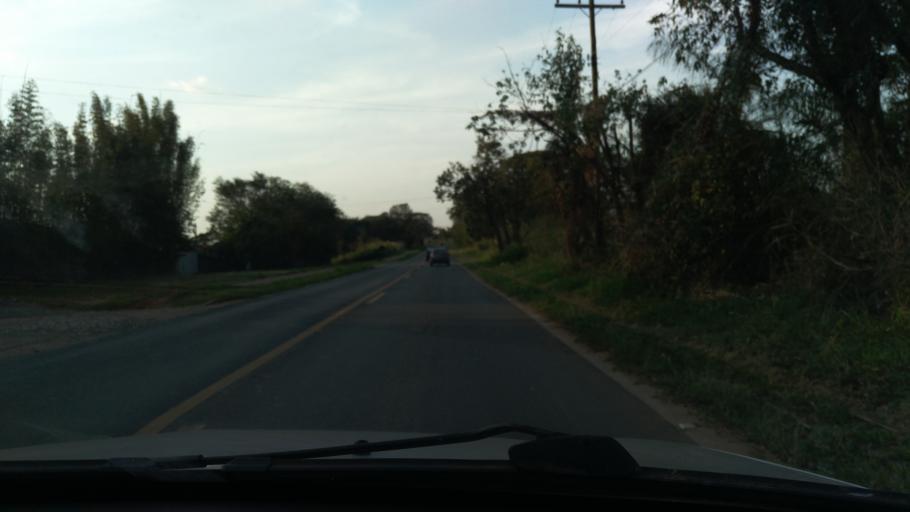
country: BR
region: Sao Paulo
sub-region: Valinhos
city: Valinhos
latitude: -23.0024
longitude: -47.0027
